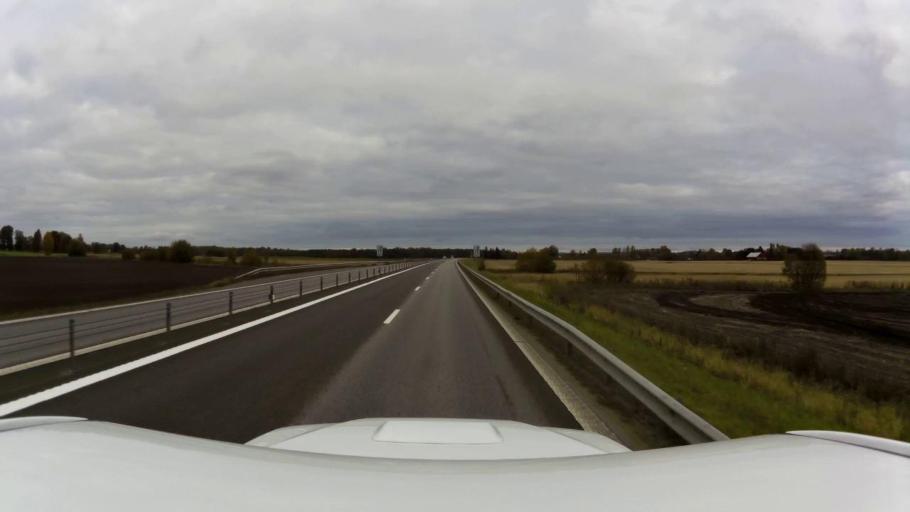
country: SE
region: OEstergoetland
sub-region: Linkopings Kommun
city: Malmslatt
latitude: 58.4473
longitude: 15.5111
